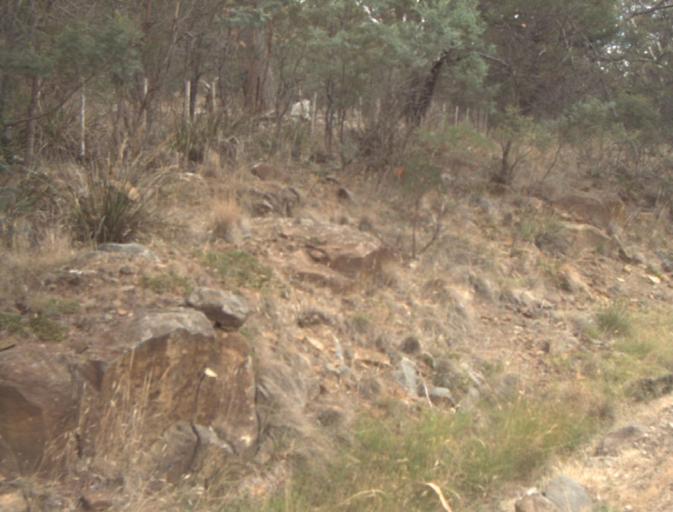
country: AU
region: Tasmania
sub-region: Northern Midlands
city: Evandale
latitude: -41.4969
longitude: 147.3848
